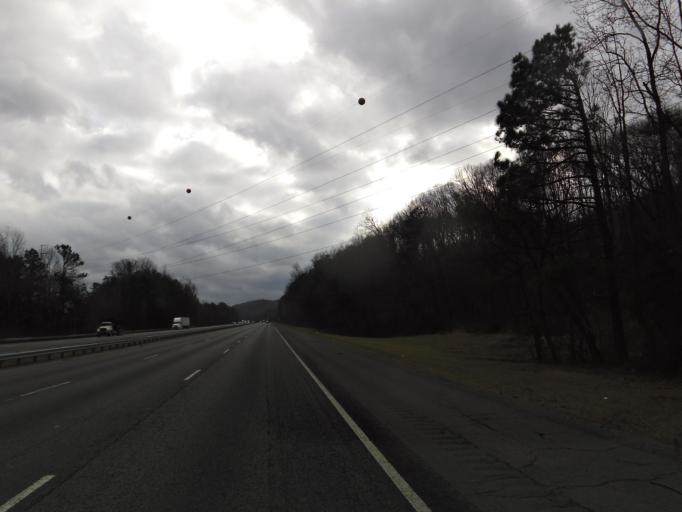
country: US
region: Georgia
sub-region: Whitfield County
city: Dalton
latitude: 34.7355
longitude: -85.0037
